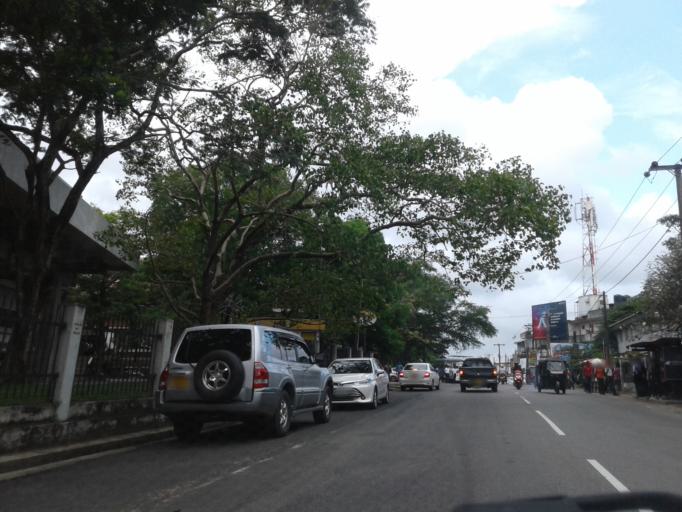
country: LK
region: Western
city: Moratuwa
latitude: 6.7952
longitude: 79.9002
